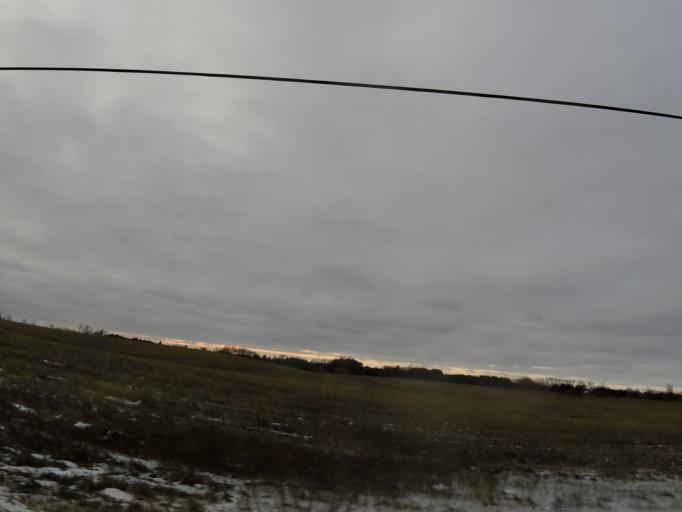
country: US
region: Minnesota
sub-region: Carver County
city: Carver
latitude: 44.7270
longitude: -93.6484
